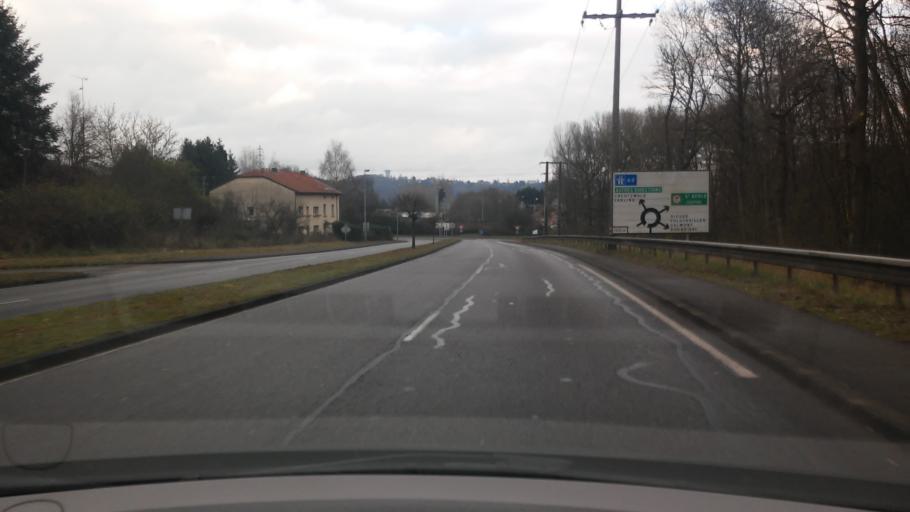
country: FR
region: Lorraine
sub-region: Departement de la Moselle
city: Saint-Avold
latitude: 49.1084
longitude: 6.6874
